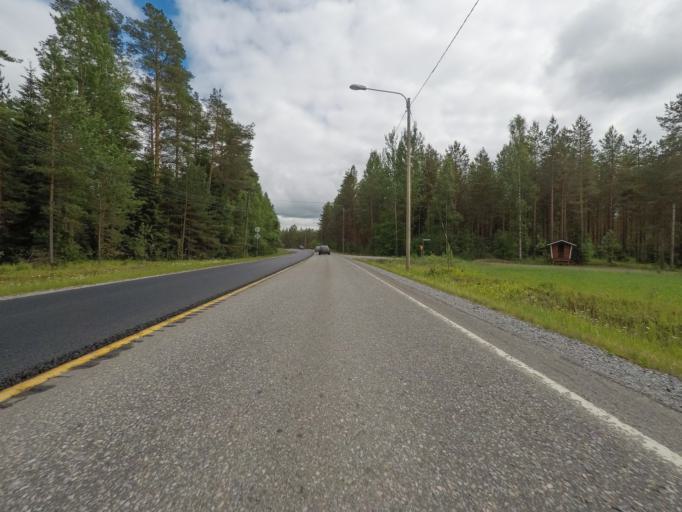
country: FI
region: Northern Savo
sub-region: Kuopio
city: Vehmersalmi
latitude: 62.9200
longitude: 28.1082
